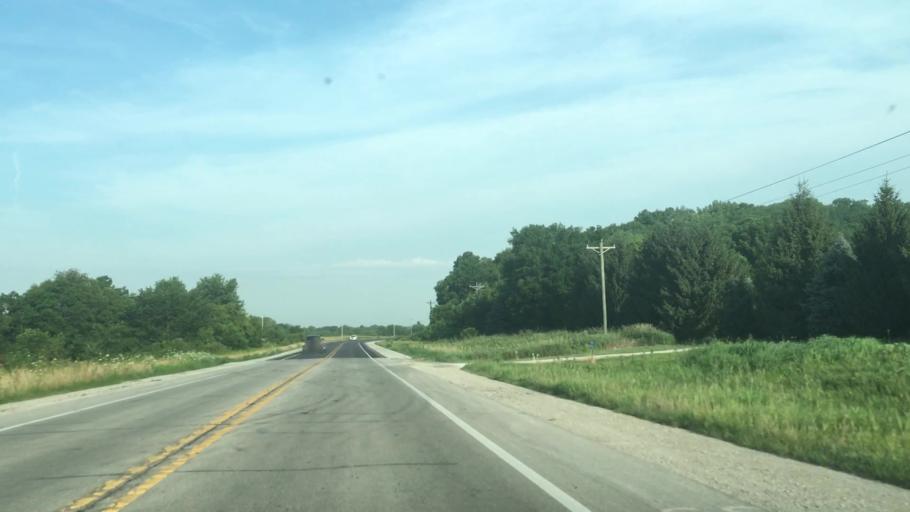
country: US
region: Iowa
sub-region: Johnson County
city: Tiffin
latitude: 41.7157
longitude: -91.7231
